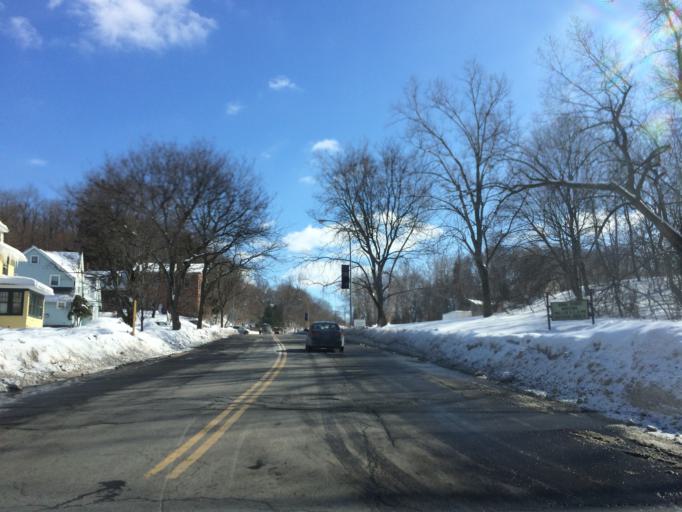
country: US
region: New York
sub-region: Monroe County
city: Rochester
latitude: 43.1353
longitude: -77.5925
